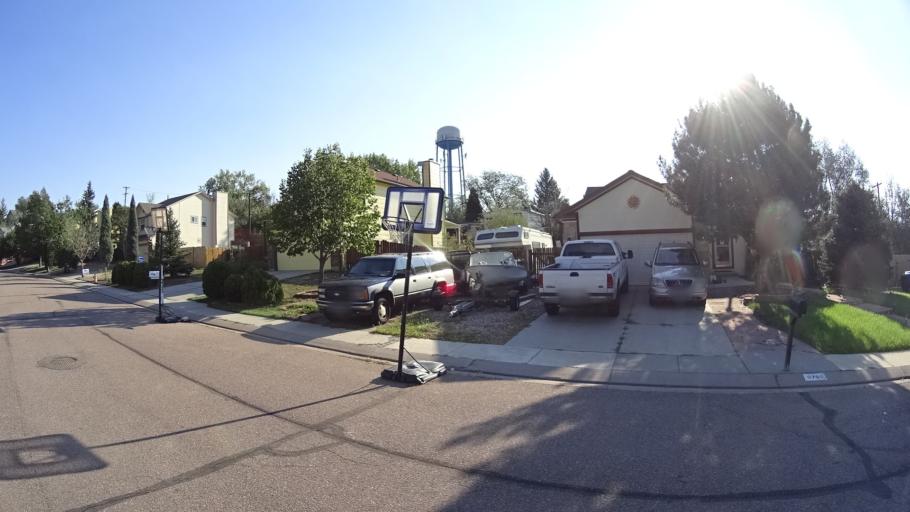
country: US
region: Colorado
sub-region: El Paso County
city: Stratmoor
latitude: 38.7774
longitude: -104.7994
